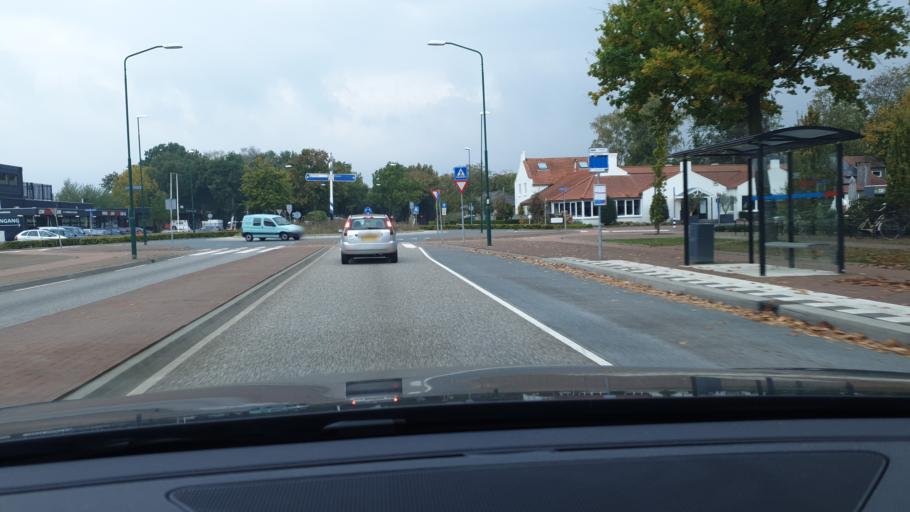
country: NL
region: North Brabant
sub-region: Gemeente Eersel
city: Eersel
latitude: 51.3651
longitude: 5.2963
